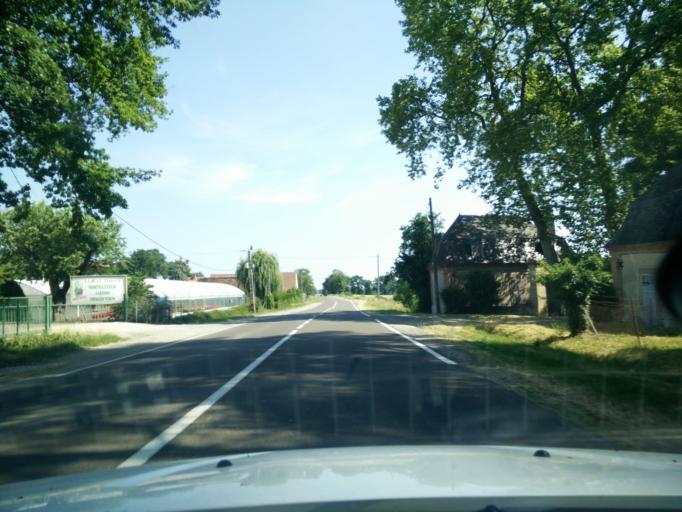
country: FR
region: Auvergne
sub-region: Departement de l'Allier
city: Toulon-sur-Allier
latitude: 46.4939
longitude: 3.3157
